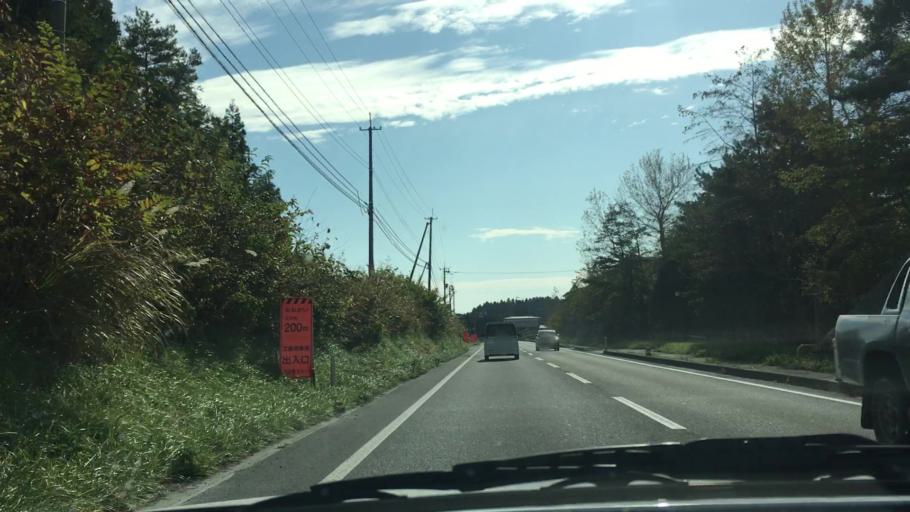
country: JP
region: Aomori
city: Hachinohe
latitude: 40.4301
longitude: 141.6908
